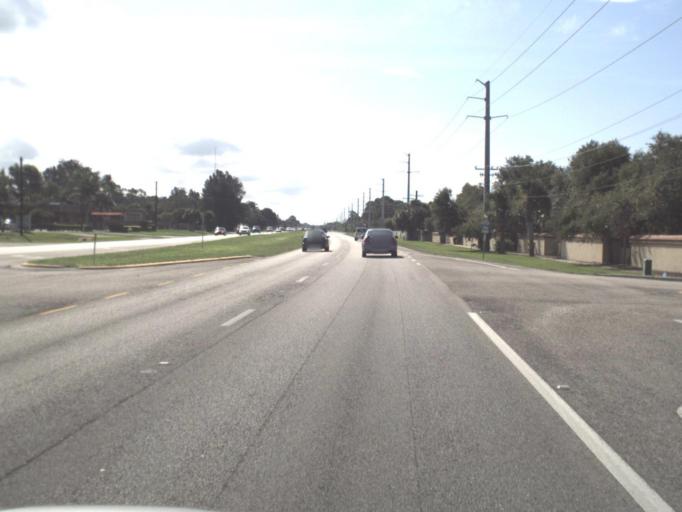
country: US
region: Florida
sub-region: Sarasota County
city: Laurel
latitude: 27.1656
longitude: -82.4759
